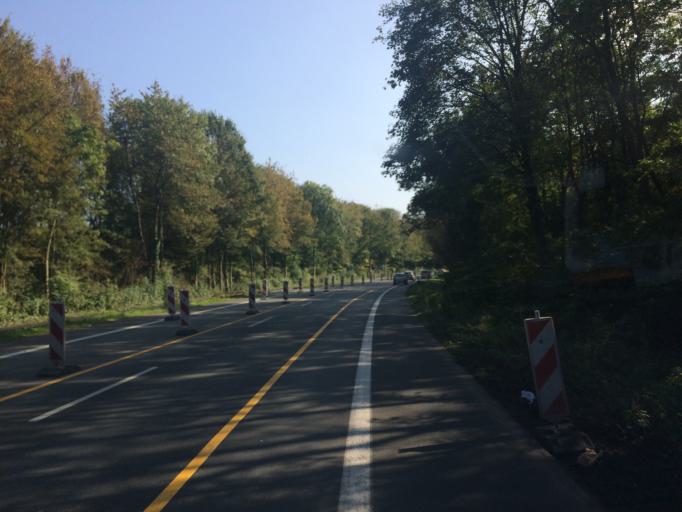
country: DE
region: North Rhine-Westphalia
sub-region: Regierungsbezirk Munster
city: Beckum
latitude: 51.7944
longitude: 8.0195
